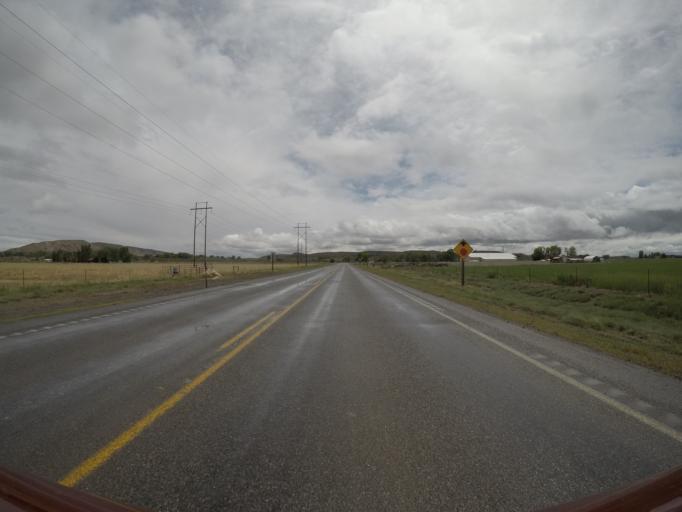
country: US
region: Wyoming
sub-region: Big Horn County
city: Lovell
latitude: 44.8433
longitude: -108.3316
